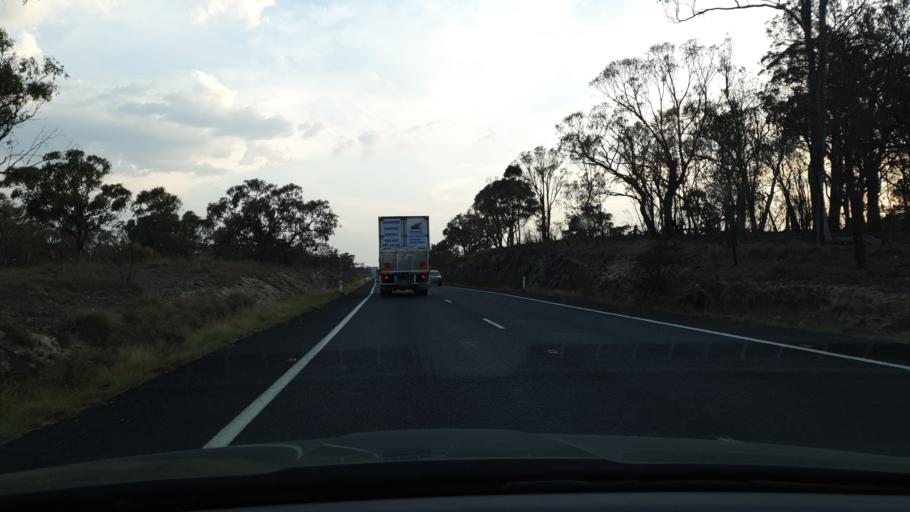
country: AU
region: New South Wales
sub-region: Glen Innes Severn
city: Glen Innes
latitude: -29.6091
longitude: 151.8653
